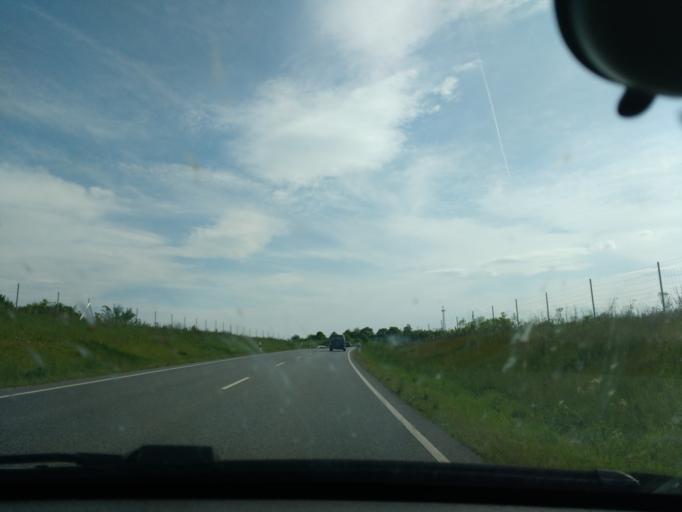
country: DE
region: Schleswig-Holstein
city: Gross Sarau
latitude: 53.7672
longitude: 10.7195
